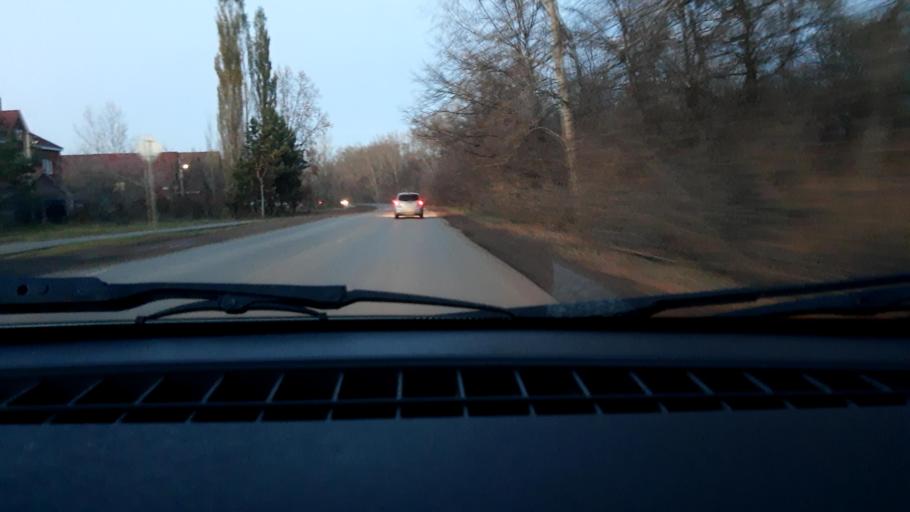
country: RU
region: Bashkortostan
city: Ufa
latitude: 54.7915
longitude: 55.9541
